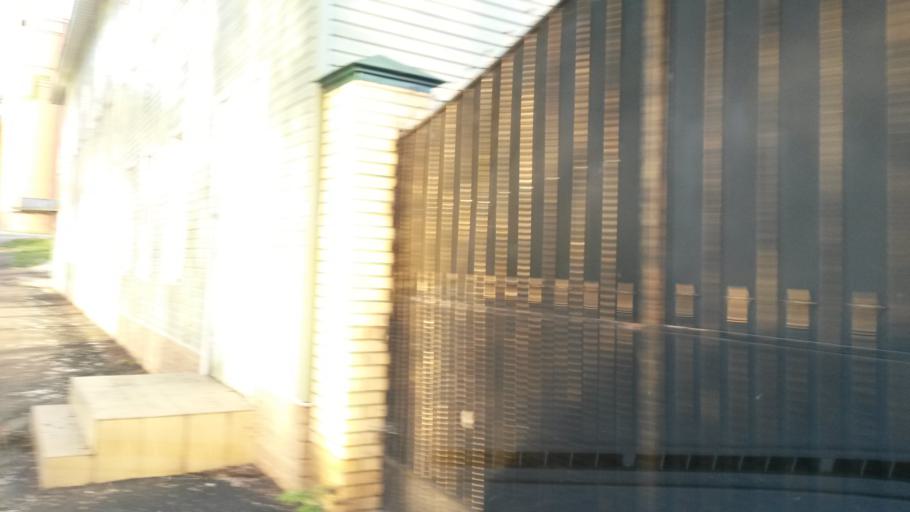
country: RU
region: Jaroslavl
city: Yaroslavl
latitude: 57.6996
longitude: 39.8278
